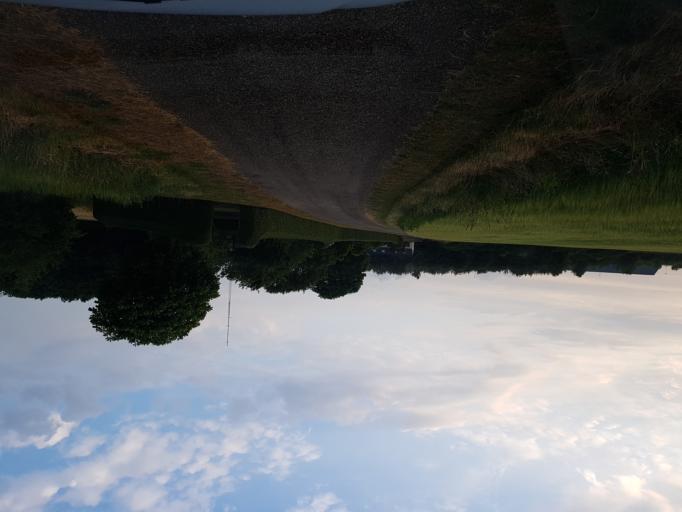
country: DK
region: South Denmark
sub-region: Esbjerg Kommune
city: Esbjerg
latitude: 55.5013
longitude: 8.4734
